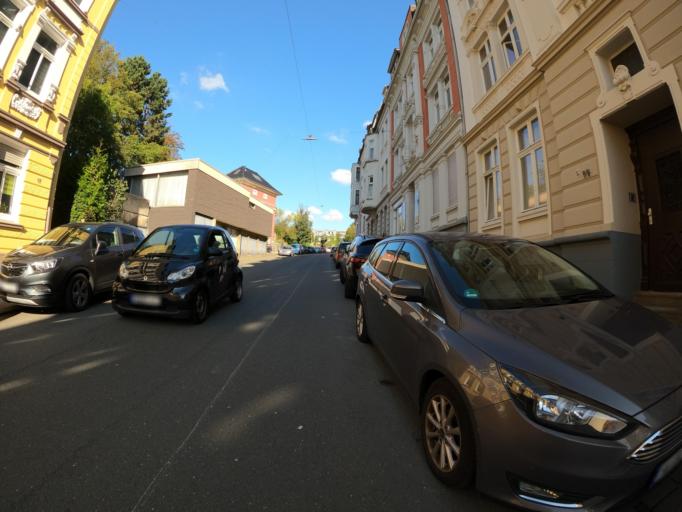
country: DE
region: North Rhine-Westphalia
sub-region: Regierungsbezirk Dusseldorf
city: Wuppertal
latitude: 51.2728
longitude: 7.1797
